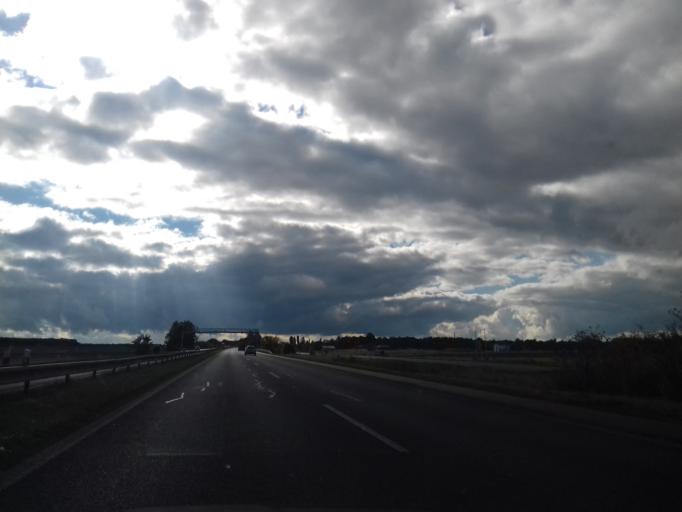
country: CZ
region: Central Bohemia
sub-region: Okres Mlada Boleslav
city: Mlada Boleslav
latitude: 50.3747
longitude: 14.8863
